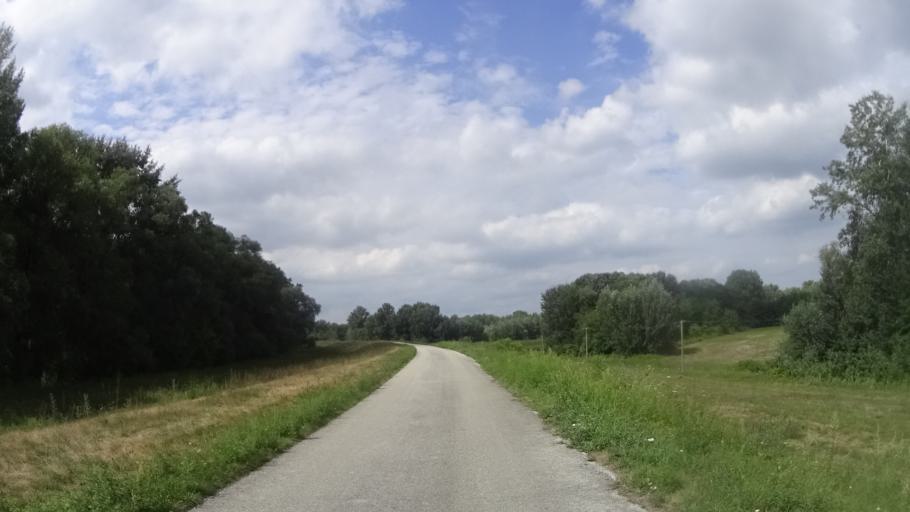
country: SK
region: Trnavsky
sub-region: Okres Dunajska Streda
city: Velky Meder
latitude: 47.7884
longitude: 17.6928
